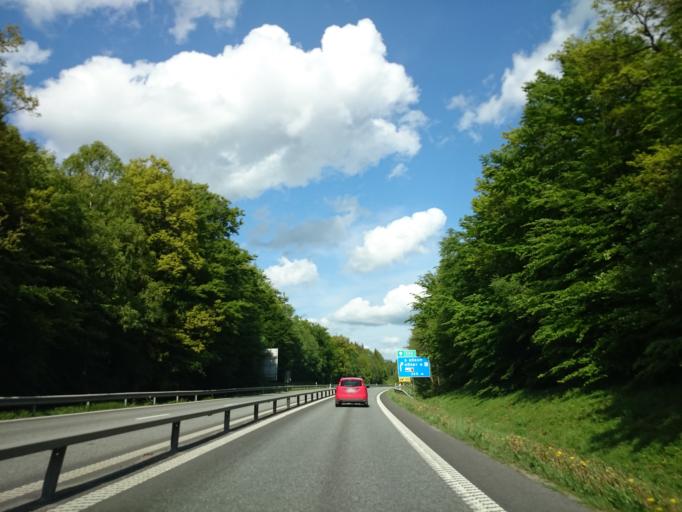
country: SE
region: Skane
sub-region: Horby Kommun
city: Hoerby
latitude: 55.8648
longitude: 13.6530
